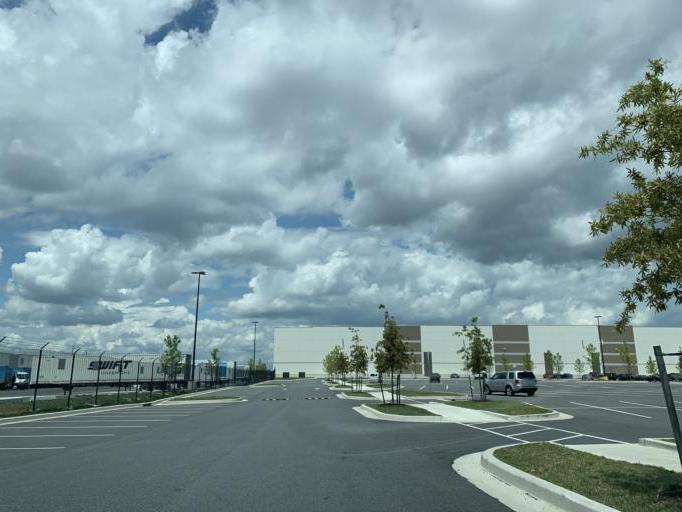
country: US
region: Maryland
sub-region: Baltimore County
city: Edgemere
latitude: 39.2275
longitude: -76.4707
